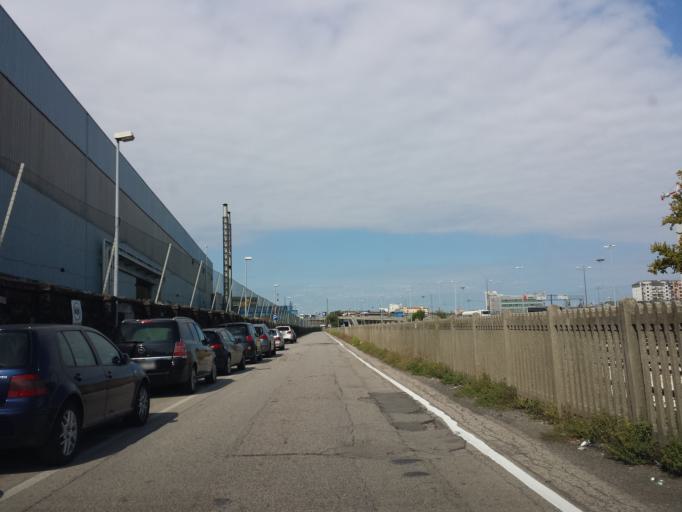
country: IT
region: Veneto
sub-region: Provincia di Venezia
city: Mestre
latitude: 45.4776
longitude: 12.2453
